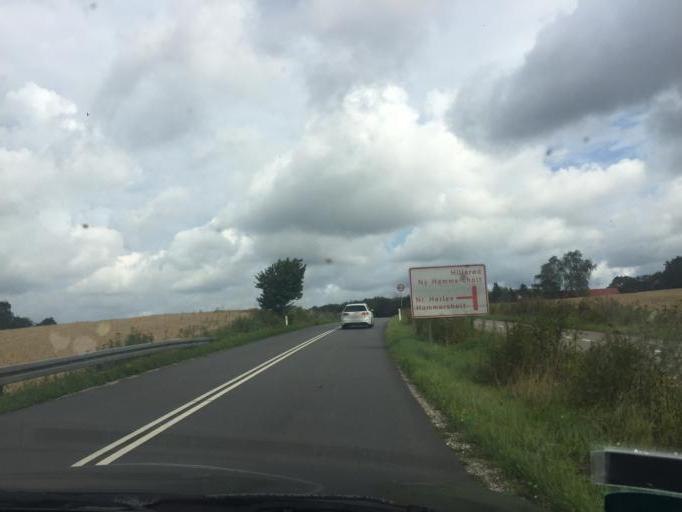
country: DK
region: Capital Region
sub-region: Allerod Kommune
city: Lillerod
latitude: 55.8993
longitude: 12.3451
